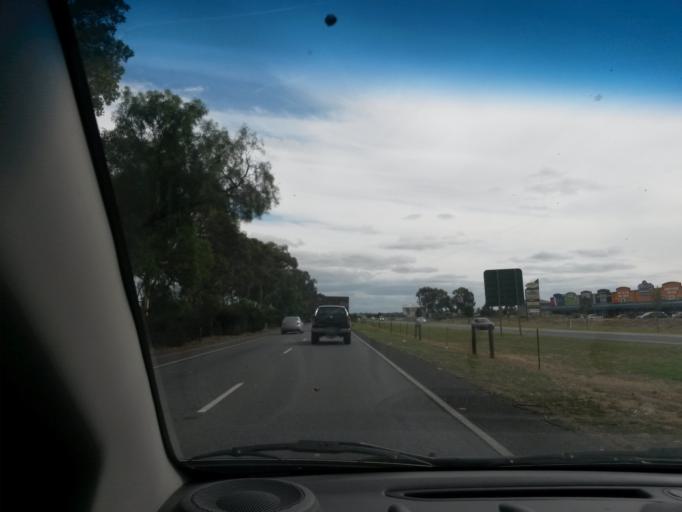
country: AU
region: South Australia
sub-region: Salisbury
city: Salisbury
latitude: -34.7952
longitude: 138.6441
